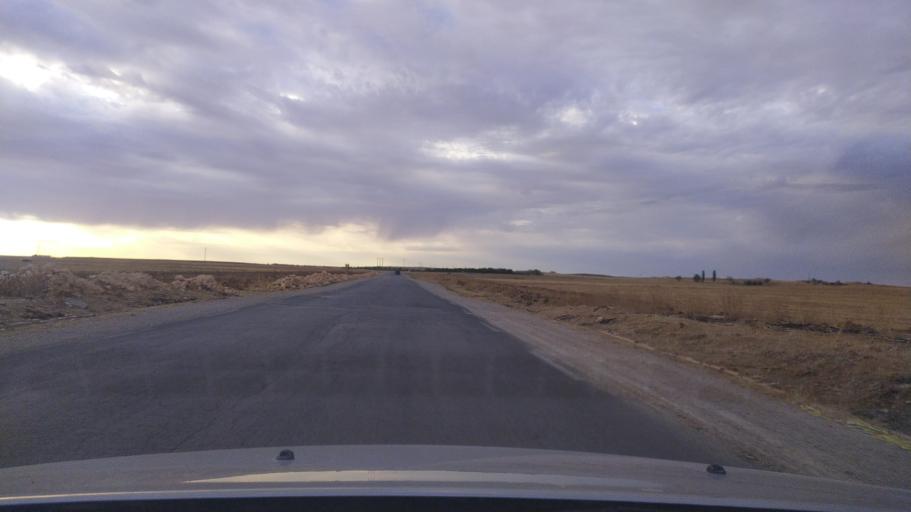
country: DZ
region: Tiaret
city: Frenda
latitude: 34.9806
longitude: 1.1489
